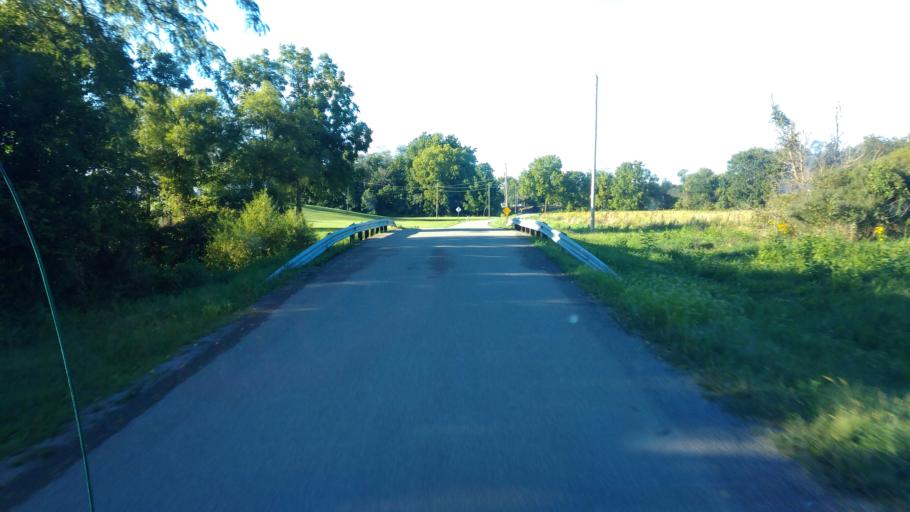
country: US
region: Ohio
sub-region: Wyandot County
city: Upper Sandusky
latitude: 40.8078
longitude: -83.3808
